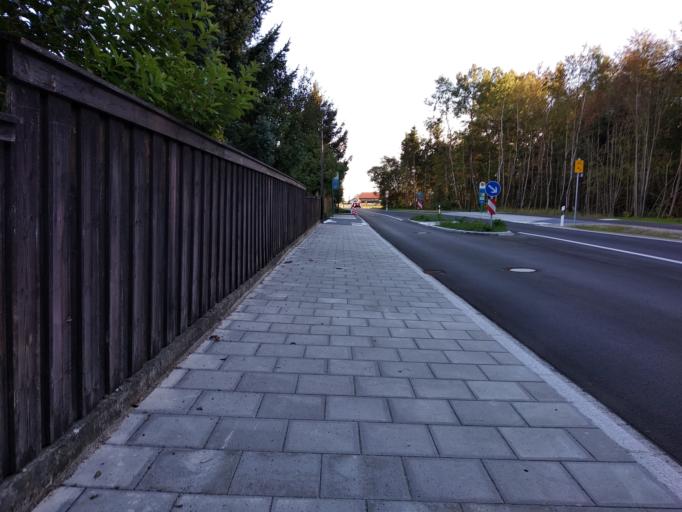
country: DE
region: Bavaria
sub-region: Upper Bavaria
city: Brunnthal
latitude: 48.0342
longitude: 11.6765
